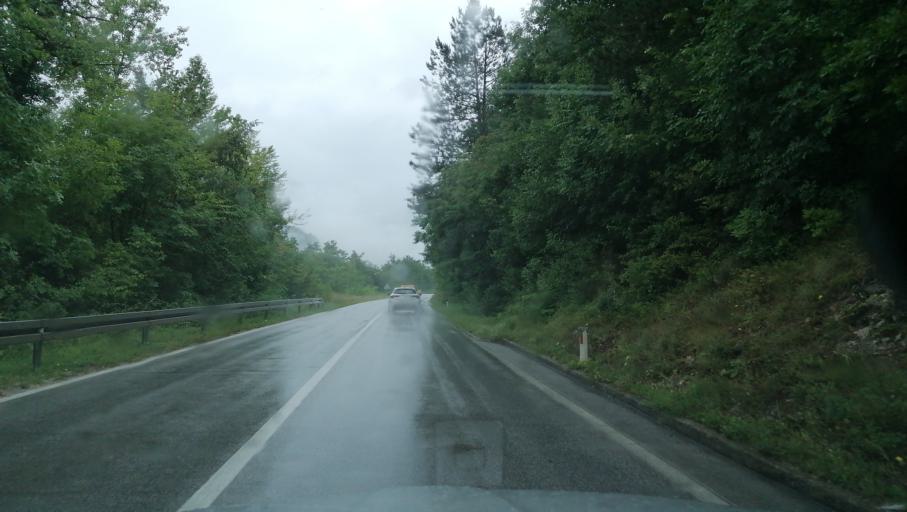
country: BA
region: Federation of Bosnia and Herzegovina
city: Gorazde
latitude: 43.6829
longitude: 19.0733
